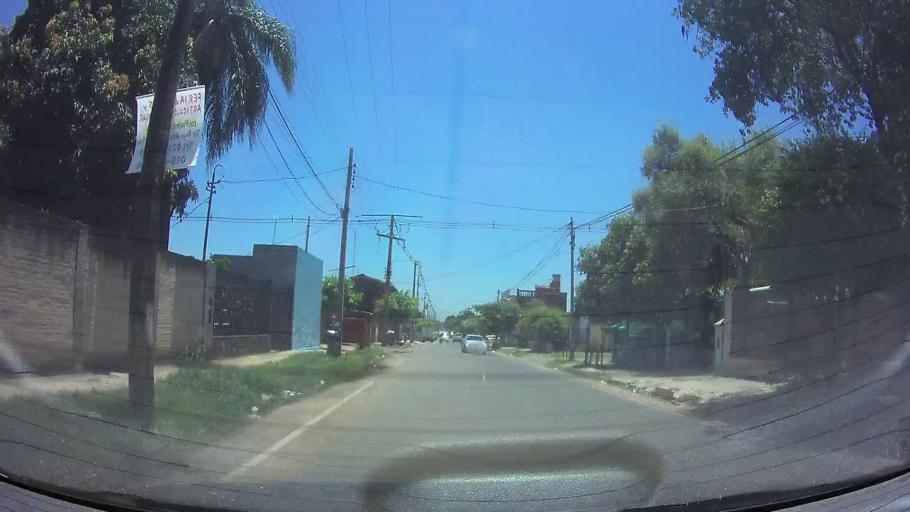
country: PY
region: Central
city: Fernando de la Mora
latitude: -25.2981
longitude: -57.5436
